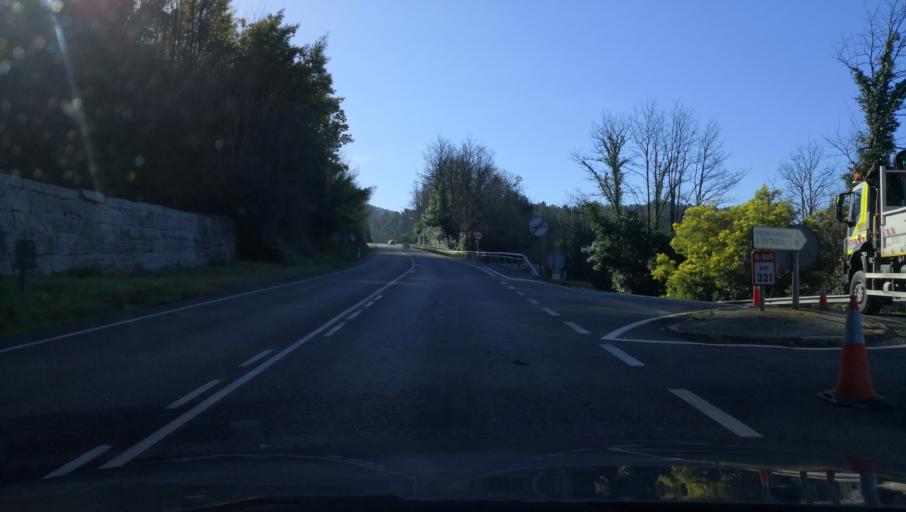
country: ES
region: Galicia
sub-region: Provincia da Coruna
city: Ribeira
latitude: 42.7744
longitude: -8.4009
